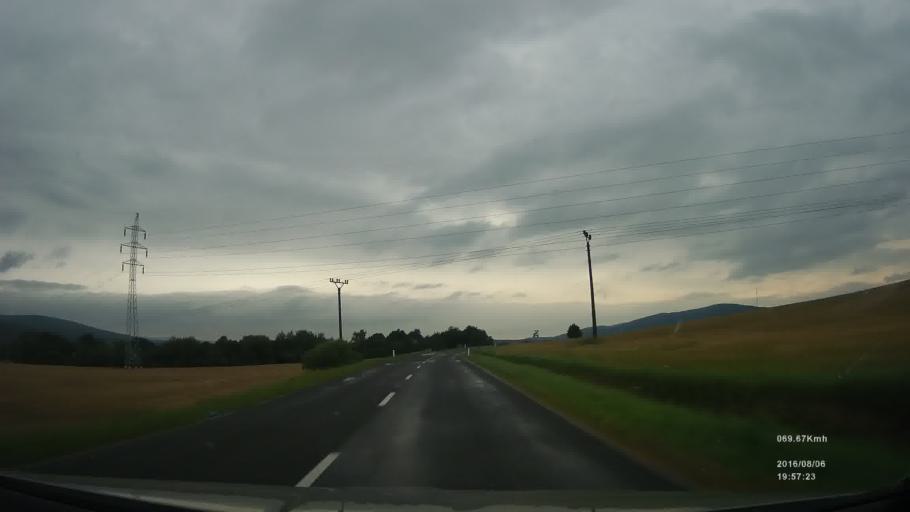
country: SK
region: Presovsky
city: Svidnik
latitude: 49.2768
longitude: 21.5748
